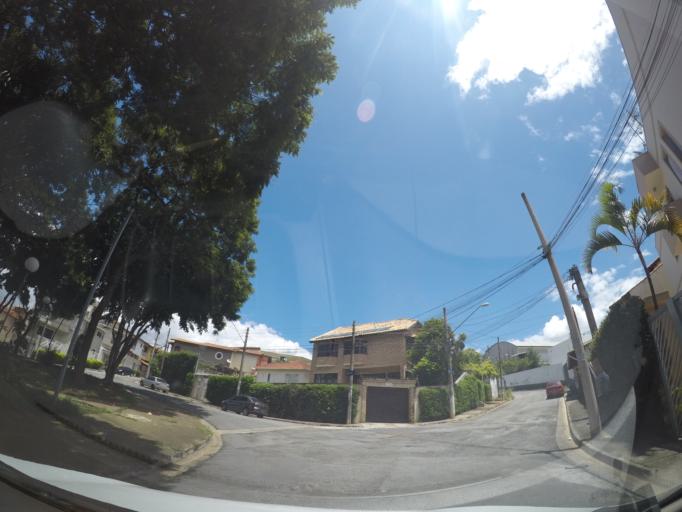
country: BR
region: Sao Paulo
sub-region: Guarulhos
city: Guarulhos
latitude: -23.4497
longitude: -46.5383
